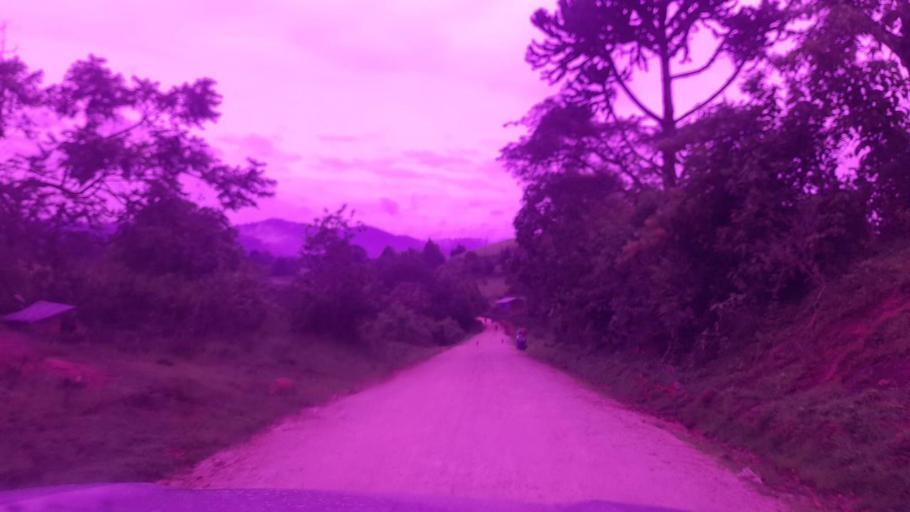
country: ET
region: Southern Nations, Nationalities, and People's Region
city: Bonga
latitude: 7.4540
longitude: 36.1273
